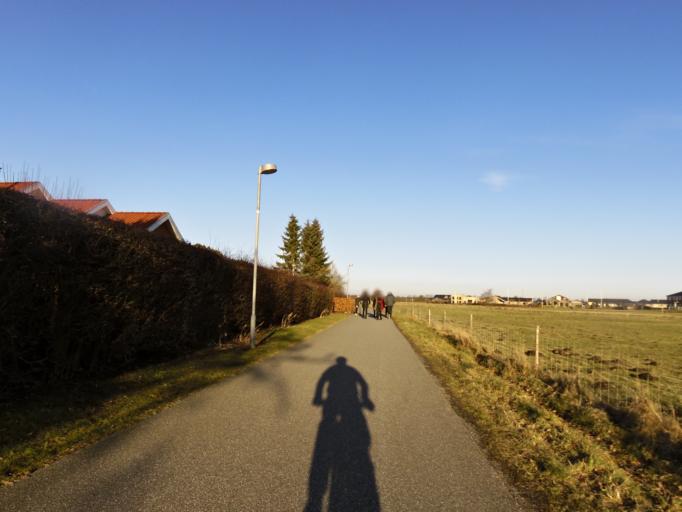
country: DK
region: South Denmark
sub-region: Esbjerg Kommune
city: Ribe
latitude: 55.3387
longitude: 8.7868
